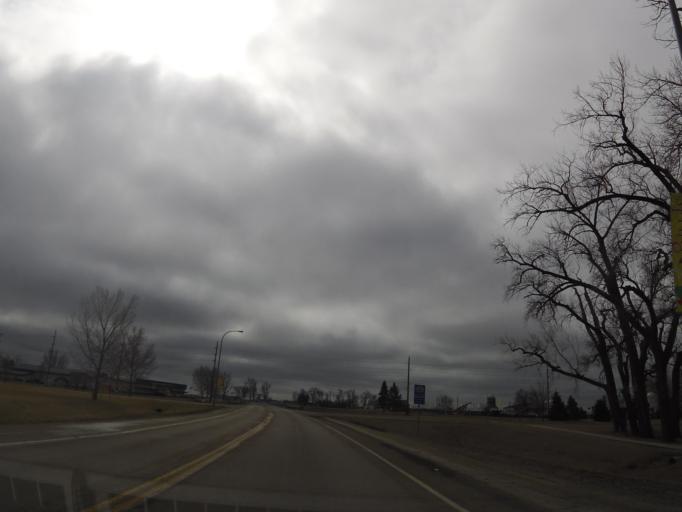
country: US
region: North Dakota
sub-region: Cass County
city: Casselton
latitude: 46.8922
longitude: -97.2122
